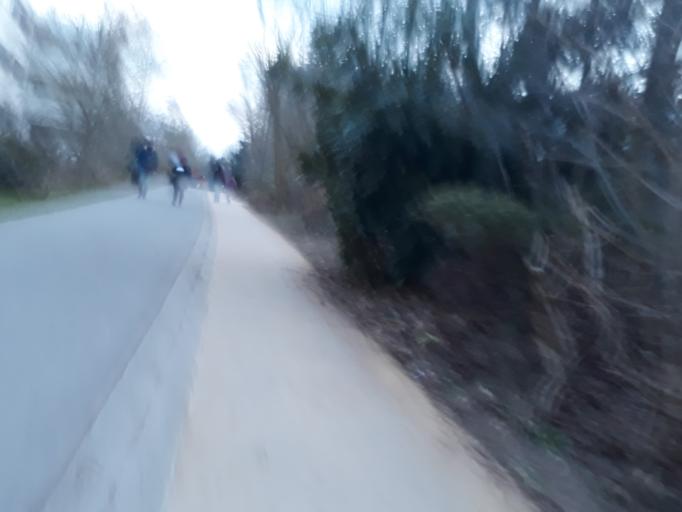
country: FR
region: Ile-de-France
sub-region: Departement des Hauts-de-Seine
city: Chatillon
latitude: 48.8069
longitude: 2.2973
